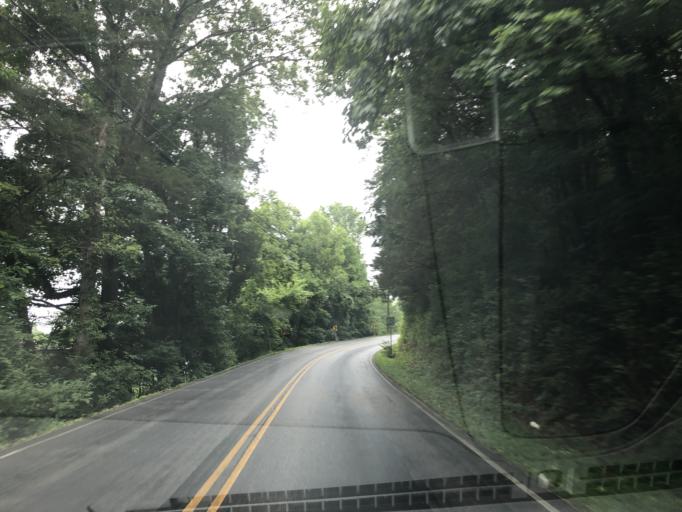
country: US
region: Tennessee
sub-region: Williamson County
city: Nolensville
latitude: 36.0306
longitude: -86.6726
